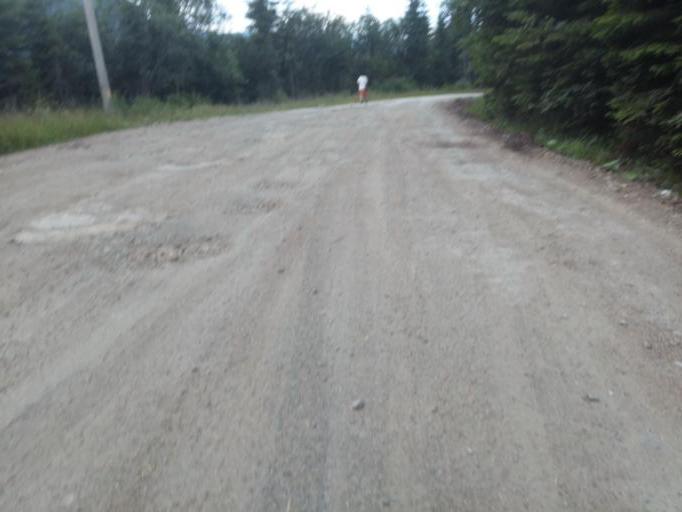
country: RO
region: Valcea
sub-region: Comuna Voineasa
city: Voineasa
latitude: 45.4400
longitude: 23.7634
